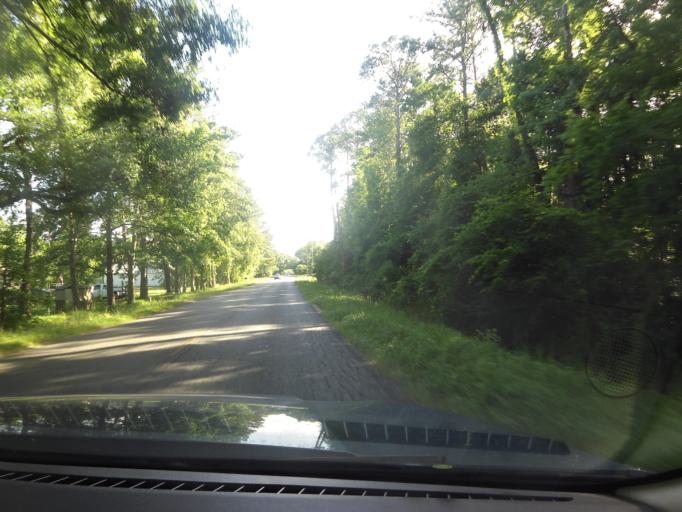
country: US
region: Florida
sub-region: Nassau County
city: Nassau Village-Ratliff
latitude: 30.5086
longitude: -81.7985
